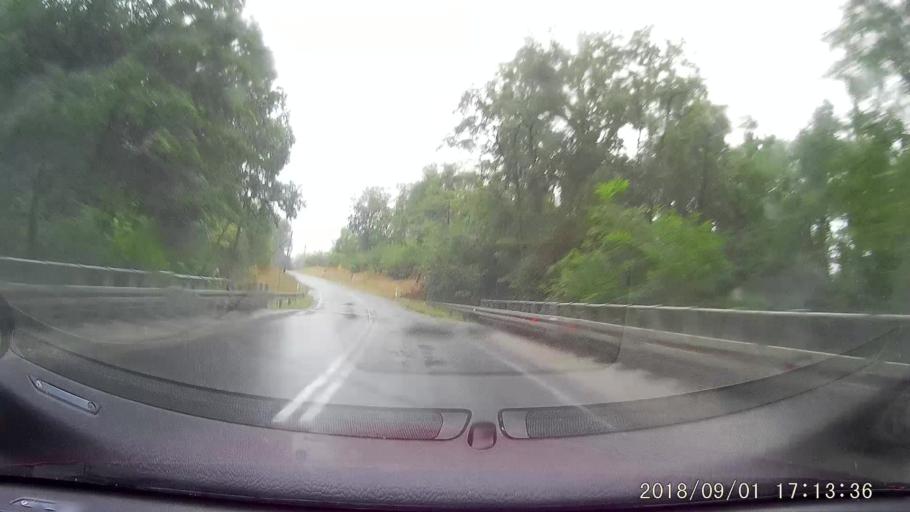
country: PL
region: Lubusz
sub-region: Powiat zielonogorski
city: Nowogrod Bobrzanski
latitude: 51.7922
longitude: 15.2493
